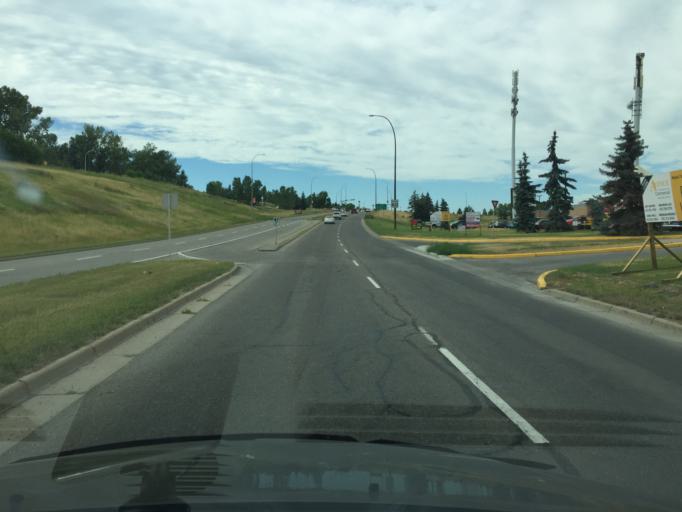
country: CA
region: Alberta
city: Calgary
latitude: 50.9280
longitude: -114.0307
